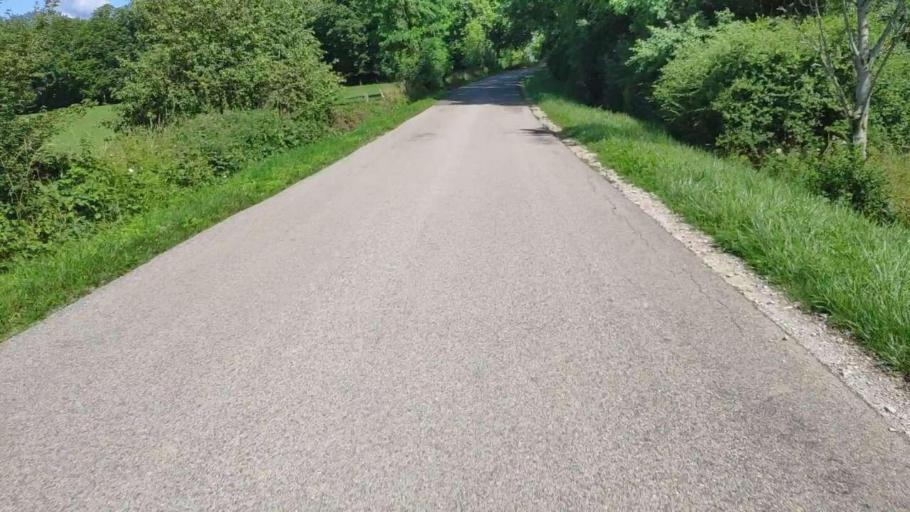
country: FR
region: Franche-Comte
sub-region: Departement du Jura
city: Bletterans
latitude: 46.8154
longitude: 5.5601
